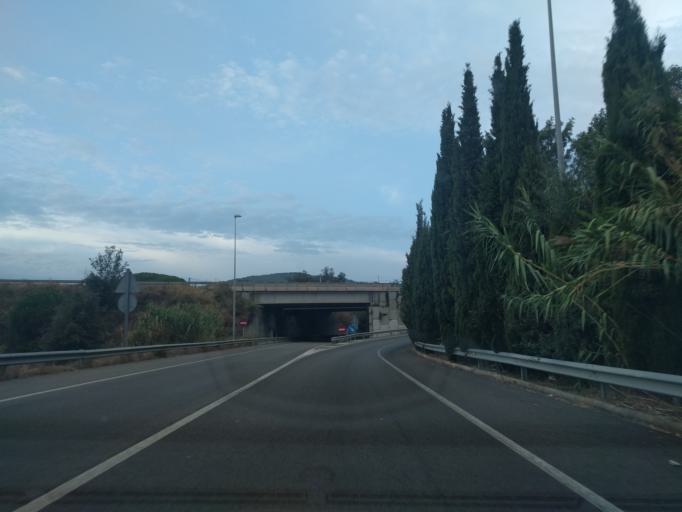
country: ES
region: Catalonia
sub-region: Provincia de Barcelona
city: Mataro
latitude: 41.5563
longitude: 2.4578
